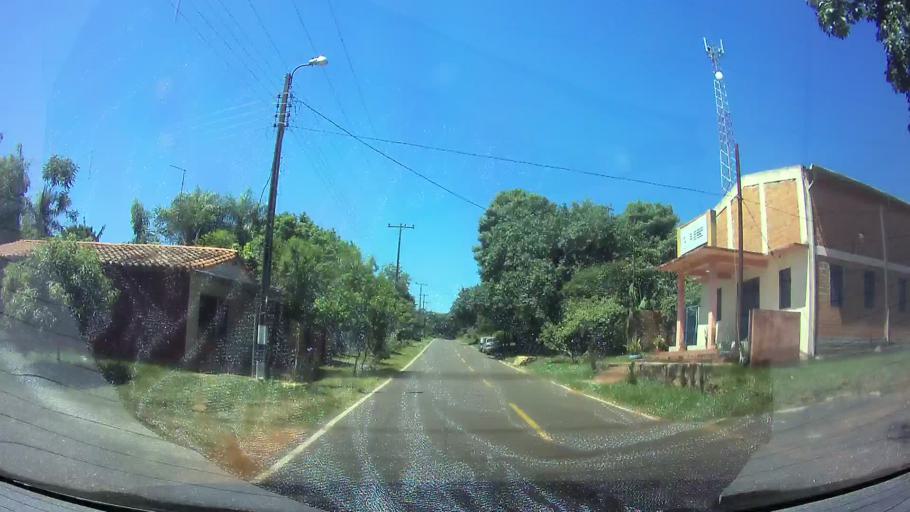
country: PY
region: Central
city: Aregua
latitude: -25.2398
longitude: -57.4353
